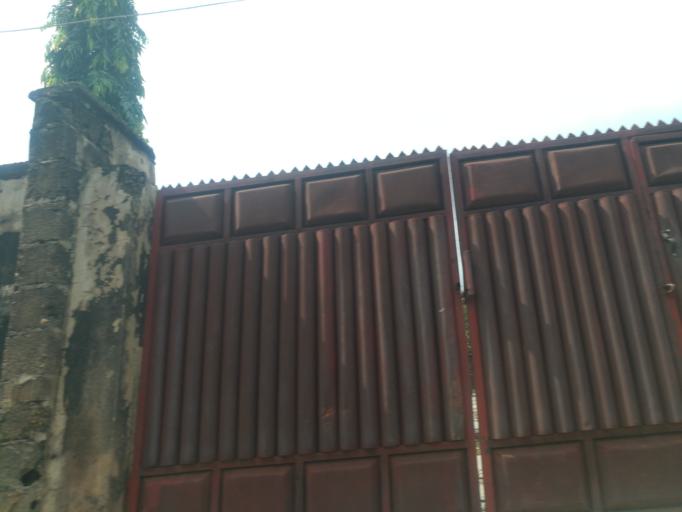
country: NG
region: Oyo
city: Moniya
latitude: 7.4610
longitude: 3.9197
